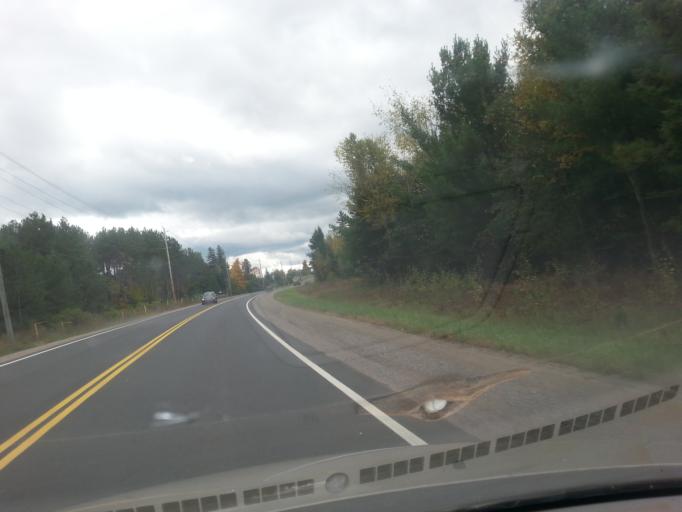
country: CA
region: Ontario
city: Pembroke
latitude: 45.5669
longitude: -77.1197
